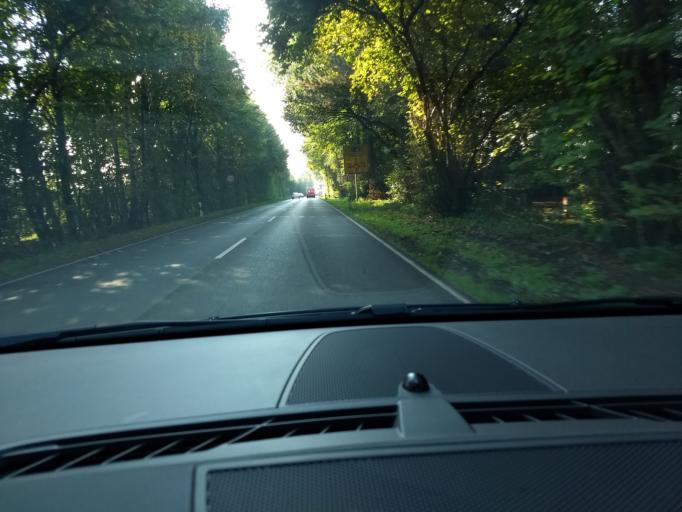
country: DE
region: North Rhine-Westphalia
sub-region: Regierungsbezirk Munster
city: Heiden
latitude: 51.8272
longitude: 6.9497
